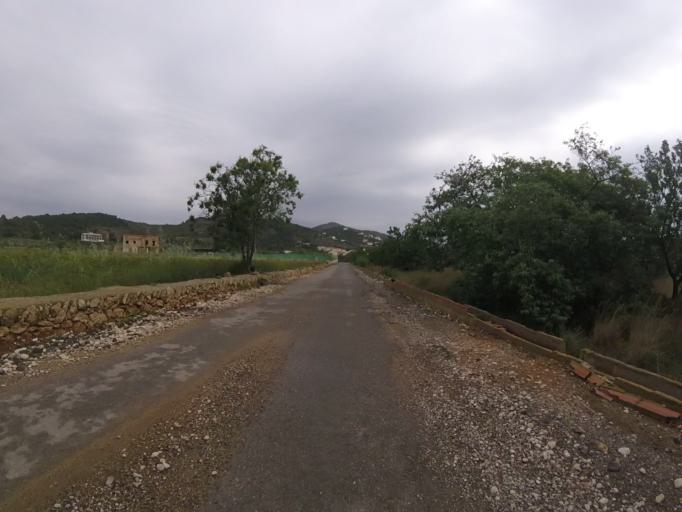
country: ES
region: Valencia
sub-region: Provincia de Castello
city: Alcoceber
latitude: 40.2445
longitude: 0.2542
